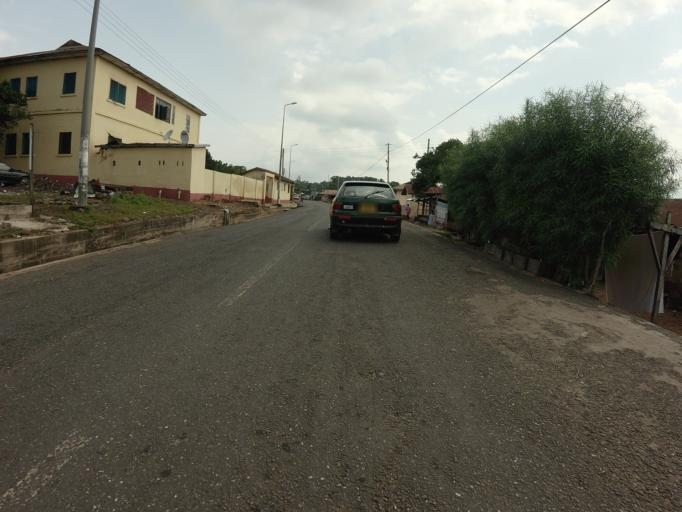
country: GH
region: Volta
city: Ho
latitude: 6.6103
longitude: 0.4735
